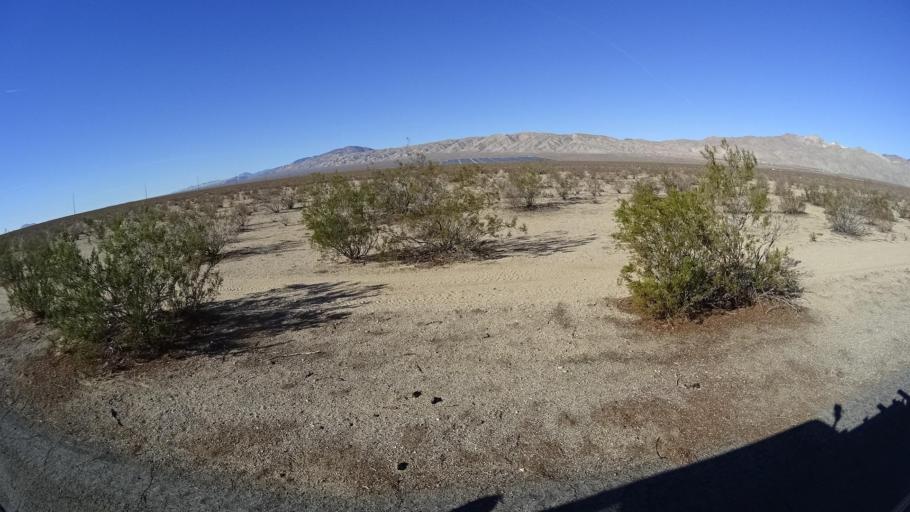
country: US
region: California
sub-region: Kern County
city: California City
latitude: 35.2040
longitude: -118.0213
